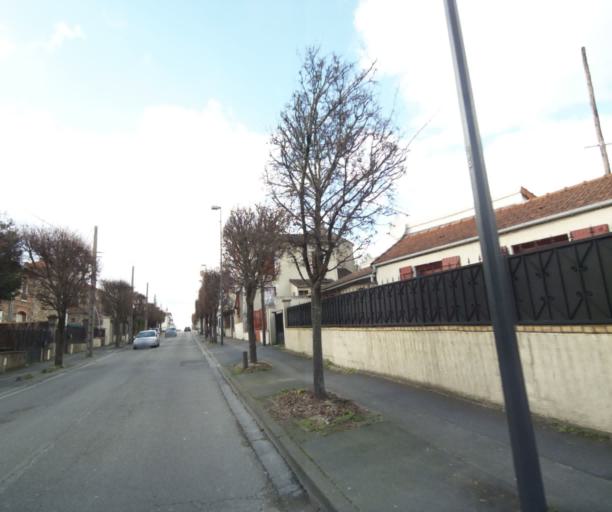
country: FR
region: Ile-de-France
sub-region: Departement de Seine-Saint-Denis
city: Pierrefitte-sur-Seine
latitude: 48.9635
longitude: 2.3556
